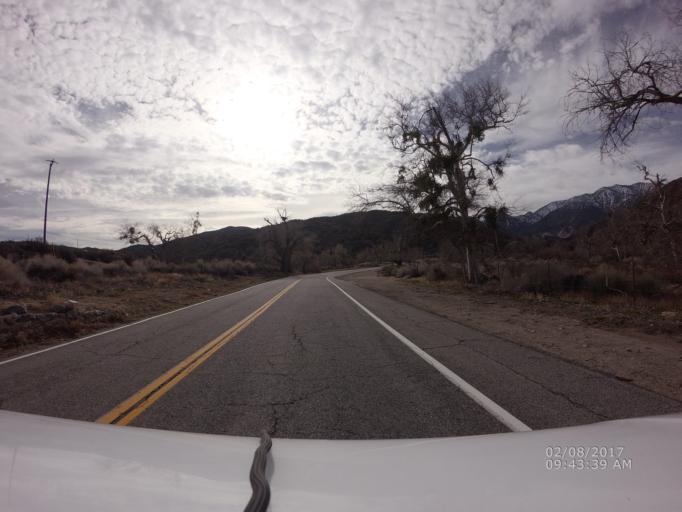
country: US
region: California
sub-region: Los Angeles County
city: Littlerock
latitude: 34.4346
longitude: -117.8356
